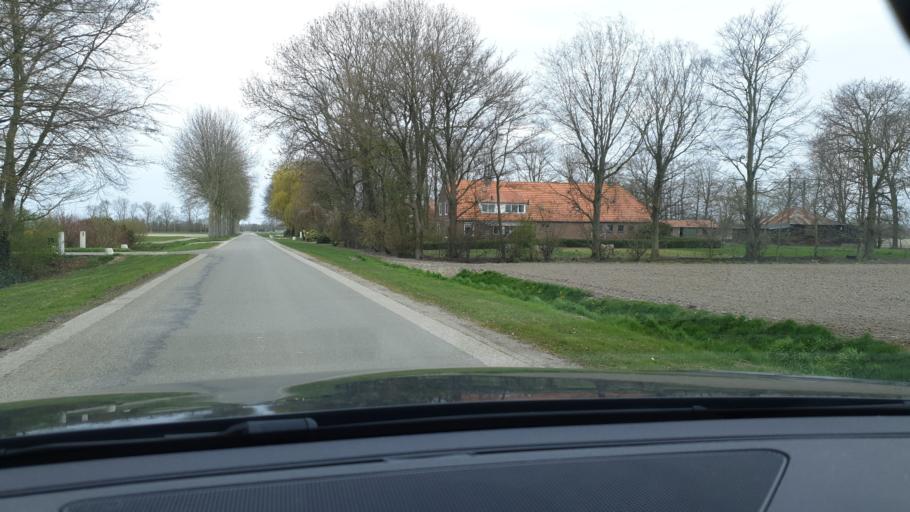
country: NL
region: Flevoland
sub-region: Gemeente Urk
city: Urk
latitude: 52.7095
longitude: 5.6641
